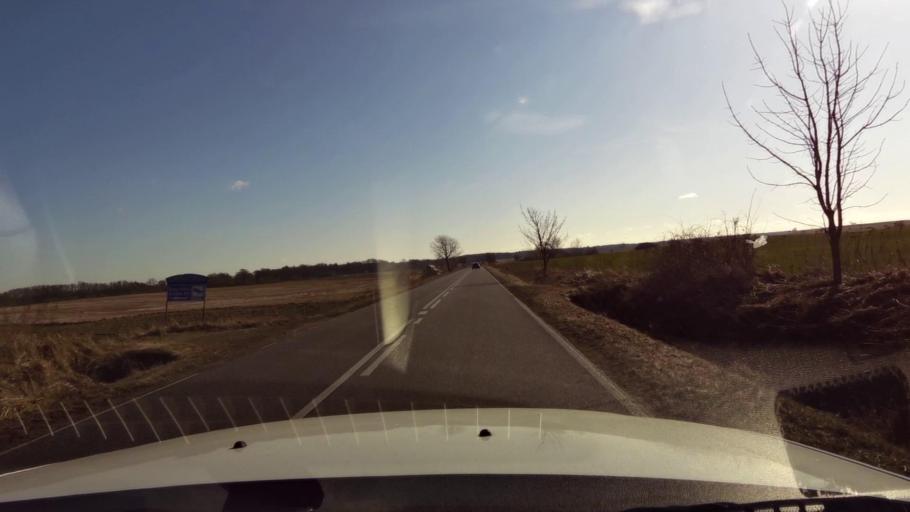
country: PL
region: West Pomeranian Voivodeship
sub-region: Powiat mysliborski
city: Nowogrodek Pomorski
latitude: 52.9882
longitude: 15.1050
